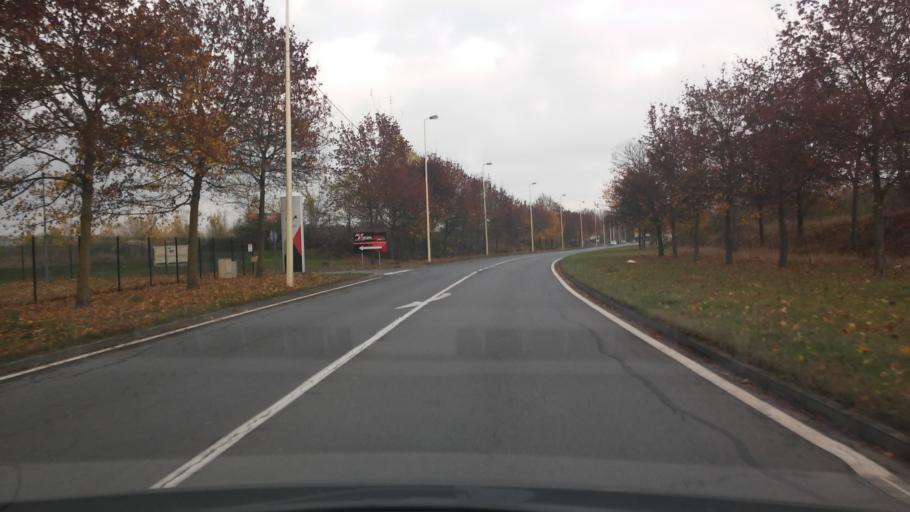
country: FR
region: Lorraine
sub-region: Departement de la Moselle
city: Terville
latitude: 49.3338
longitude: 6.1549
